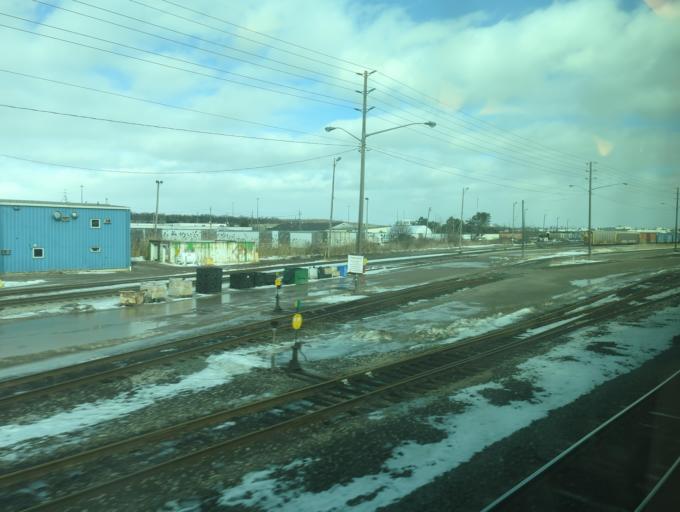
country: CA
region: Ontario
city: Oakville
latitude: 43.4665
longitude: -79.6725
